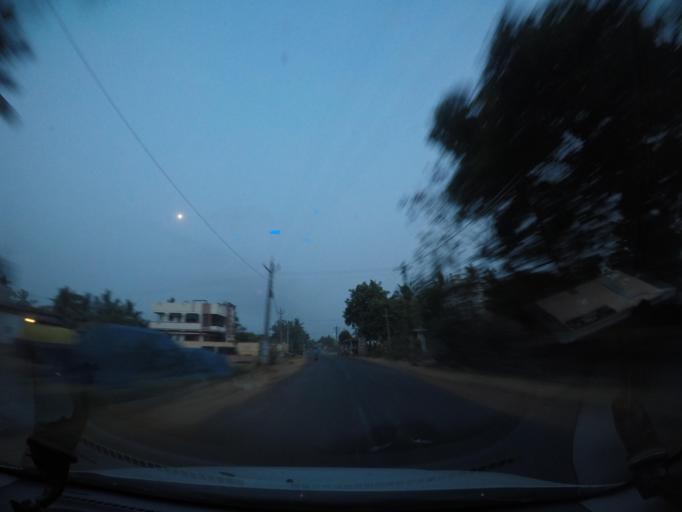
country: IN
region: Andhra Pradesh
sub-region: West Godavari
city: Tadepallegudem
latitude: 16.7823
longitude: 81.4245
